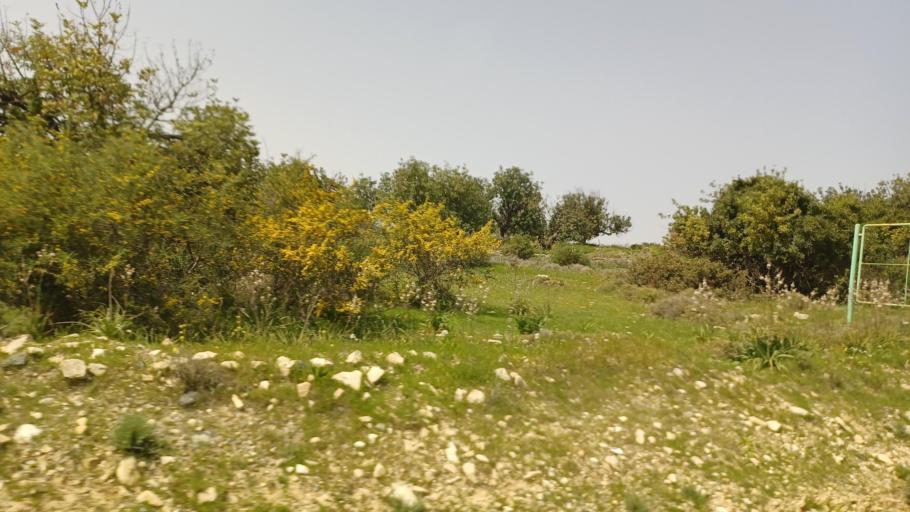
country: CY
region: Limassol
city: Pissouri
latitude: 34.7259
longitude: 32.7374
